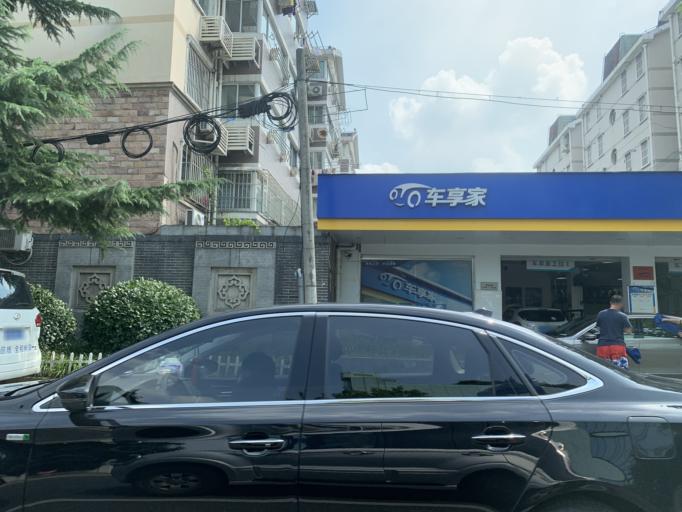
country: CN
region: Shanghai Shi
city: Luwan
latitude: 31.1822
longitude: 121.4931
